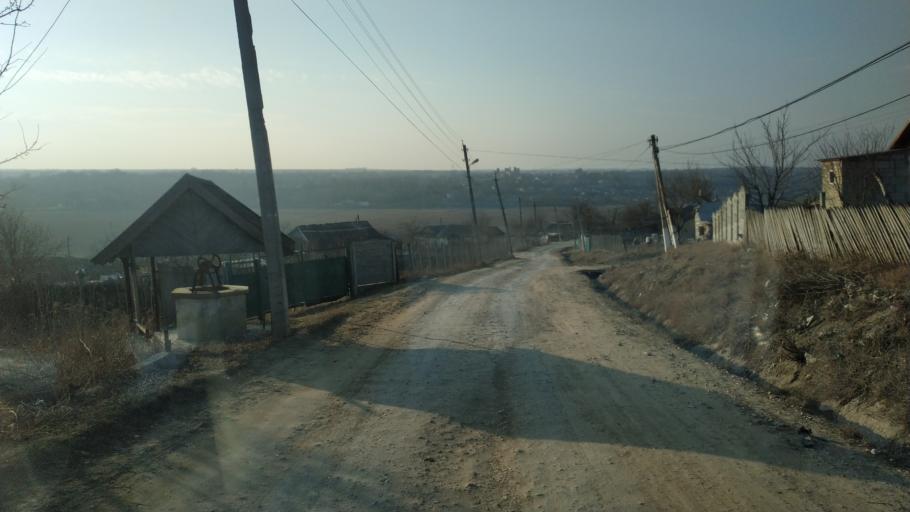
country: MD
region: Hincesti
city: Dancu
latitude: 46.7672
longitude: 28.3575
